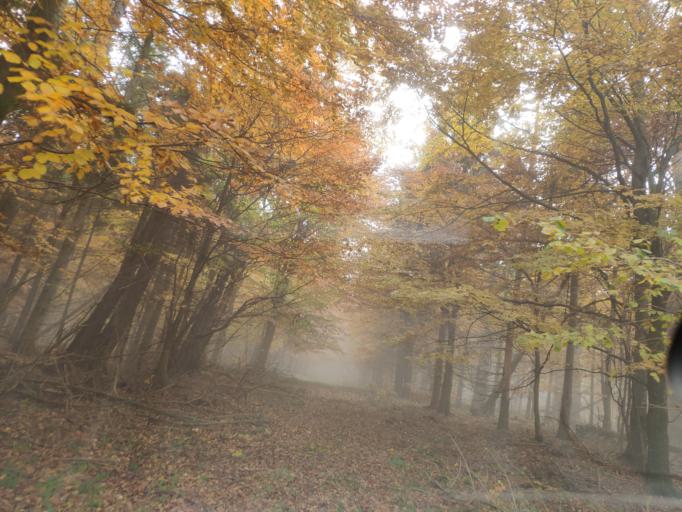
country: SK
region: Kosicky
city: Medzev
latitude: 48.7379
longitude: 20.9976
